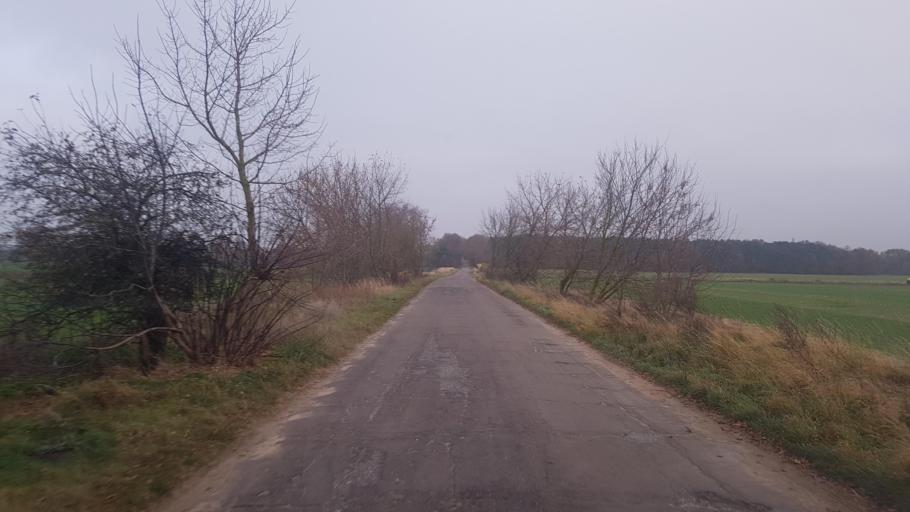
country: DE
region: Brandenburg
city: Gross Kreutz
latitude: 52.3726
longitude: 12.8097
